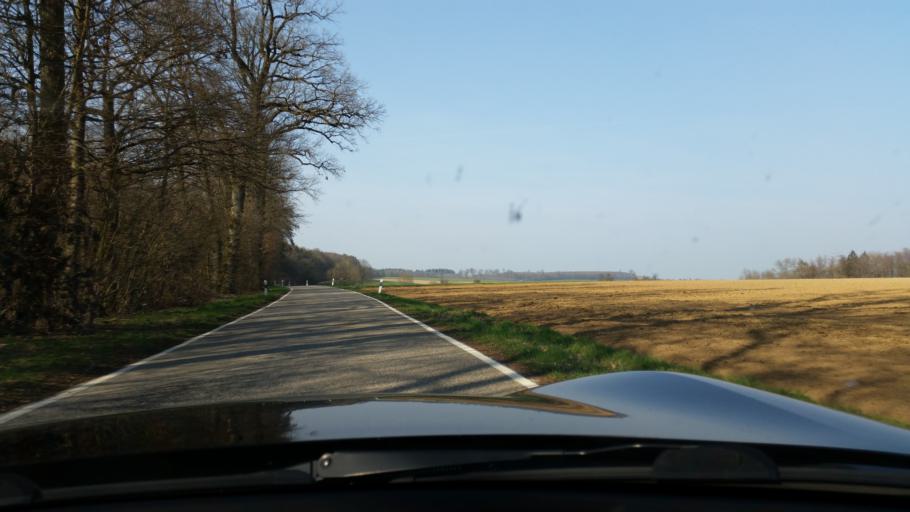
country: DE
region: Baden-Wuerttemberg
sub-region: Regierungsbezirk Stuttgart
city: Mockmuhl
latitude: 49.3460
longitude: 9.3761
